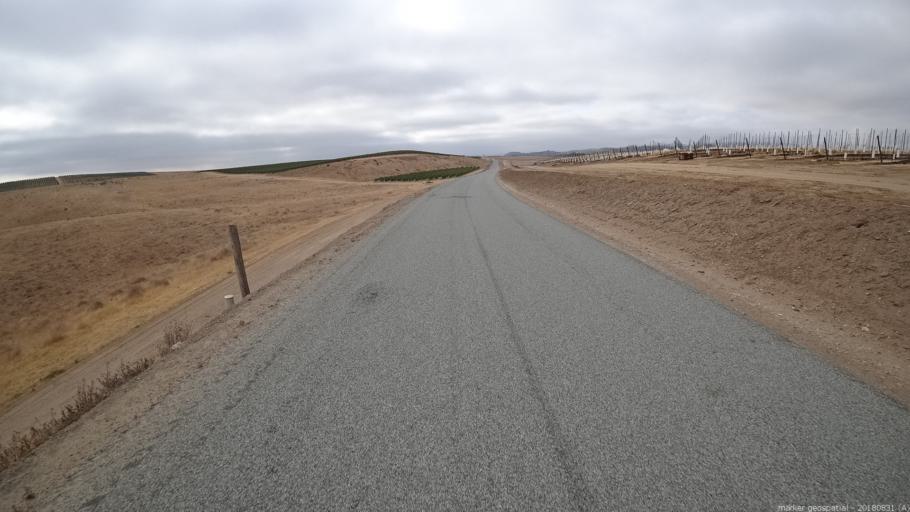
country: US
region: California
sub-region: Monterey County
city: King City
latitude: 36.1656
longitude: -121.1146
